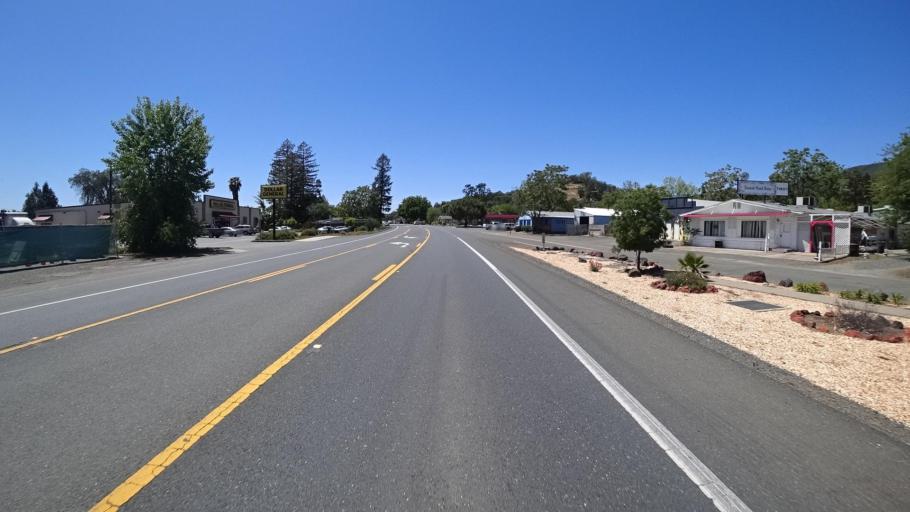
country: US
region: California
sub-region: Lake County
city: Nice
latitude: 39.1229
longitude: -122.8434
